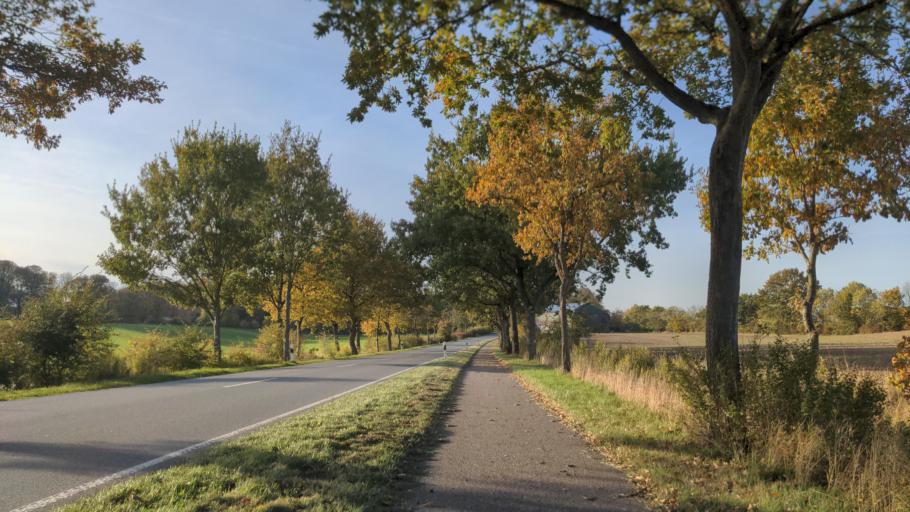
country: DE
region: Schleswig-Holstein
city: Kirchnuchel
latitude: 54.2020
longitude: 10.6859
